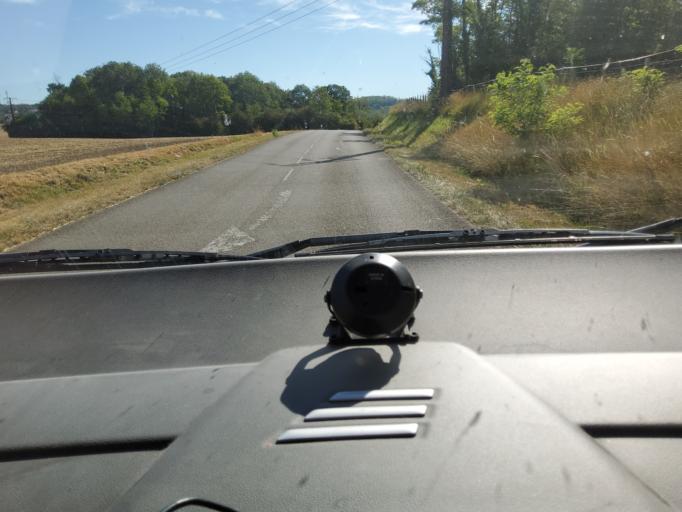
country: FR
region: Franche-Comte
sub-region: Departement du Jura
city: Champvans
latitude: 47.1050
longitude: 5.4516
